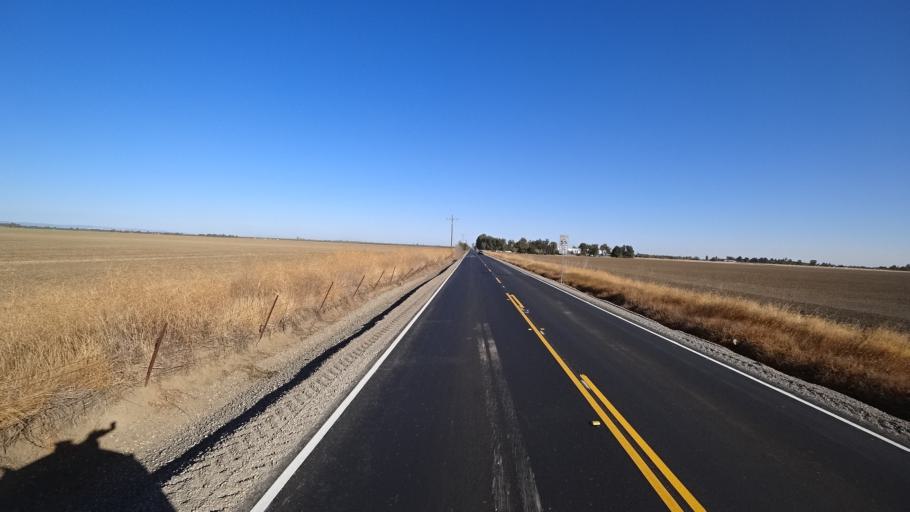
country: US
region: California
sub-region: Yolo County
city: Davis
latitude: 38.5618
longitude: -121.7862
